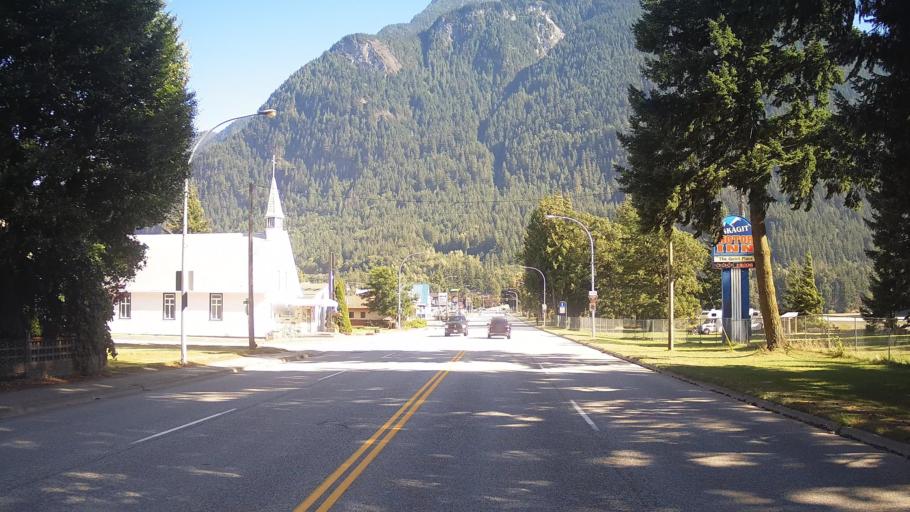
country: CA
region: British Columbia
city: Hope
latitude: 49.3812
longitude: -121.4466
